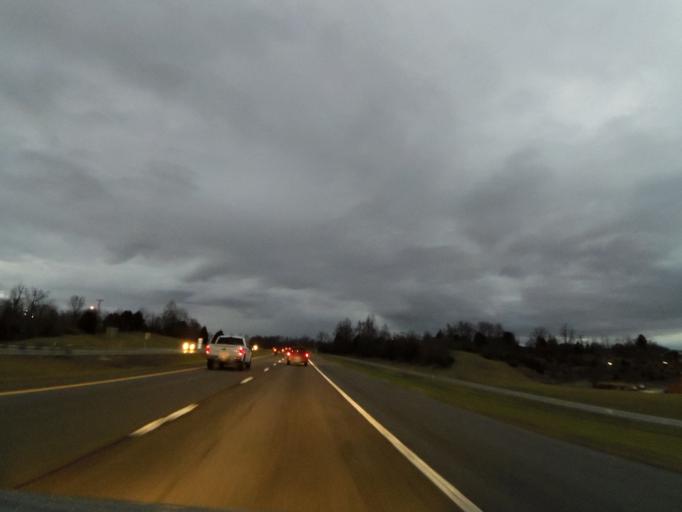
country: US
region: Tennessee
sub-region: Washington County
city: Oak Grove
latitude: 36.3787
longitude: -82.4264
